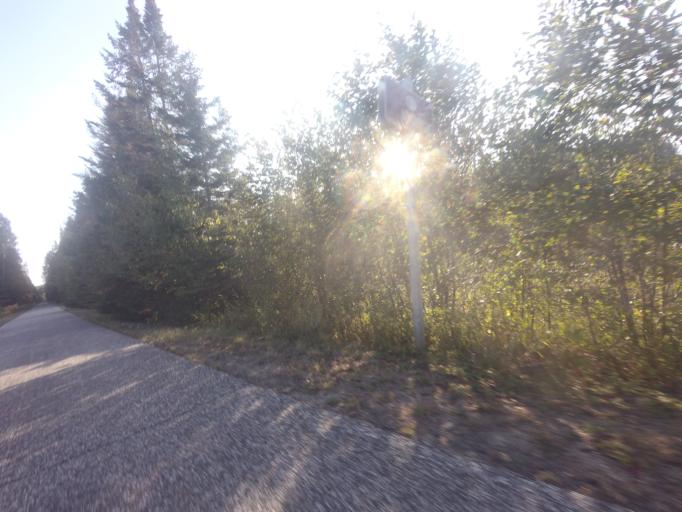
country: CA
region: Quebec
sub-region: Laurentides
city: Riviere-Rouge
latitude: 46.4275
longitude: -74.9436
